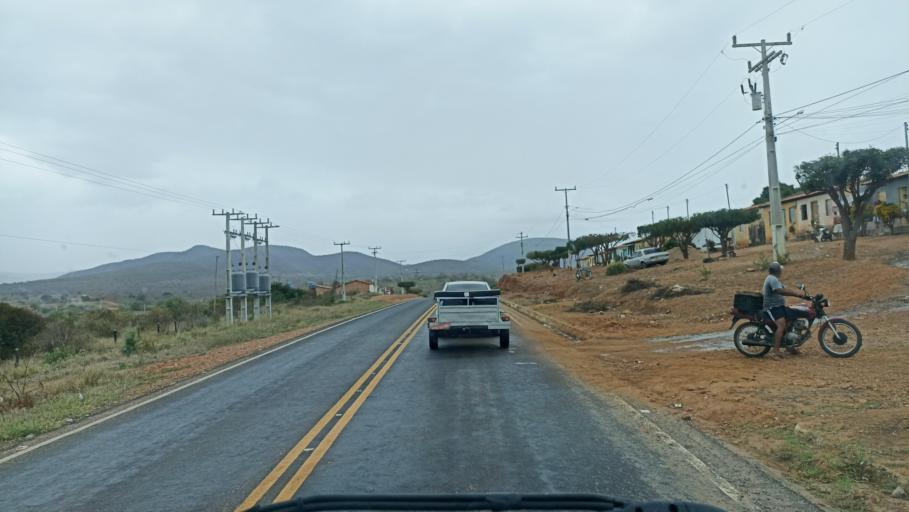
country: BR
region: Bahia
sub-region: Maracas
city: Maracas
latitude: -13.0482
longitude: -40.7438
